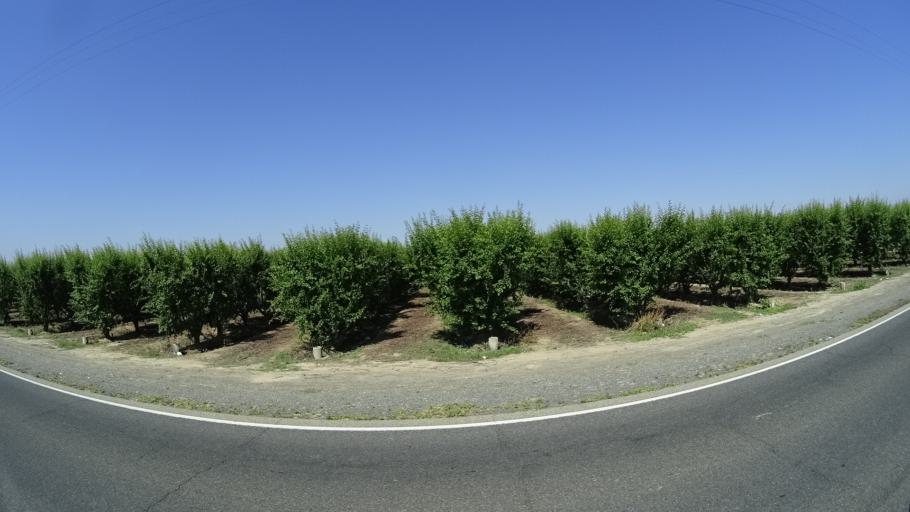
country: US
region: California
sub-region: Fresno County
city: Kingsburg
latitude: 36.4627
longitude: -119.5644
